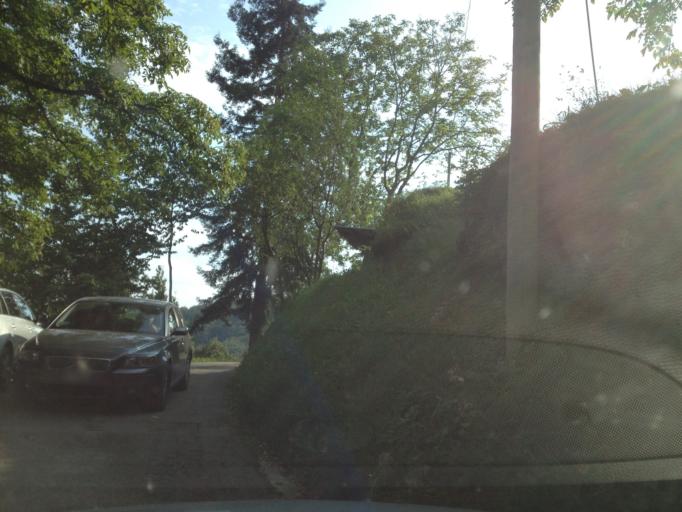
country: IT
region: Veneto
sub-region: Provincia di Vicenza
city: Posina
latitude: 45.8073
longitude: 11.2610
